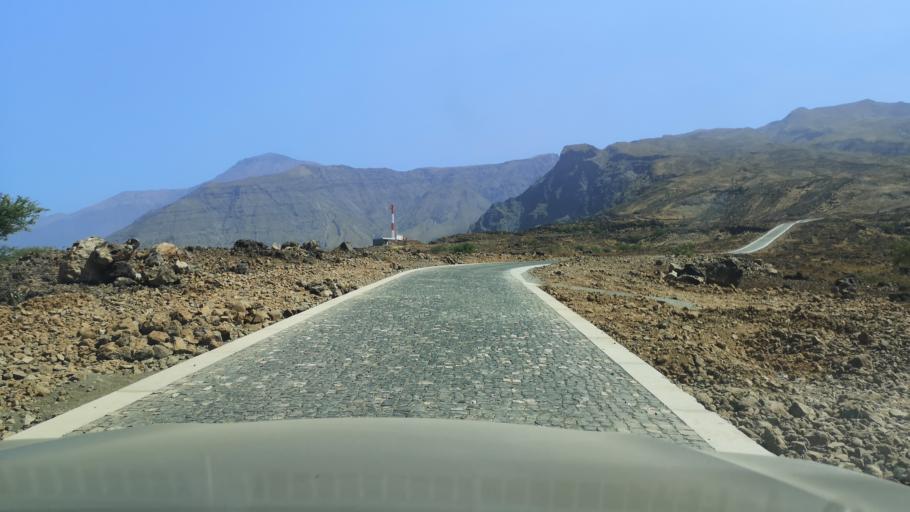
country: CV
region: Porto Novo
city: Porto Novo
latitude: 16.9412
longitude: -25.3147
